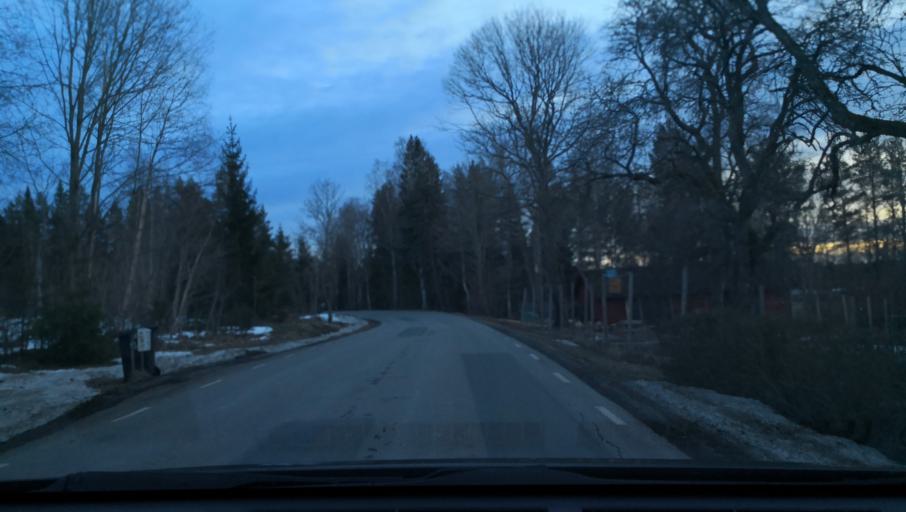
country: SE
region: Uppsala
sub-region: Osthammars Kommun
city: Osterbybruk
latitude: 60.2577
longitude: 17.9476
